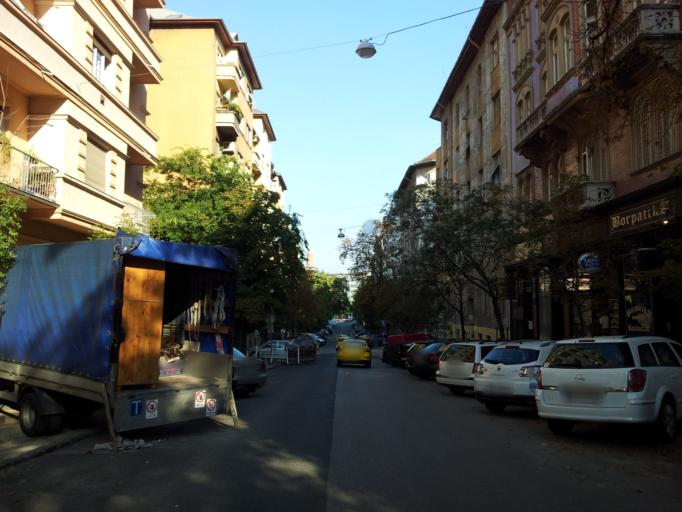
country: HU
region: Budapest
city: Budapest IX. keruelet
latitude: 47.4797
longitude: 19.0519
